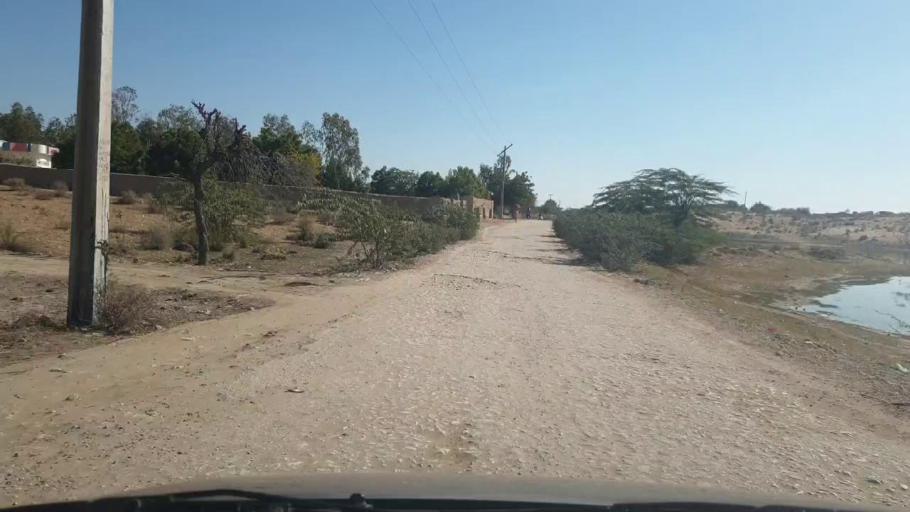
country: PK
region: Sindh
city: Bozdar
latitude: 27.0630
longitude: 68.6249
